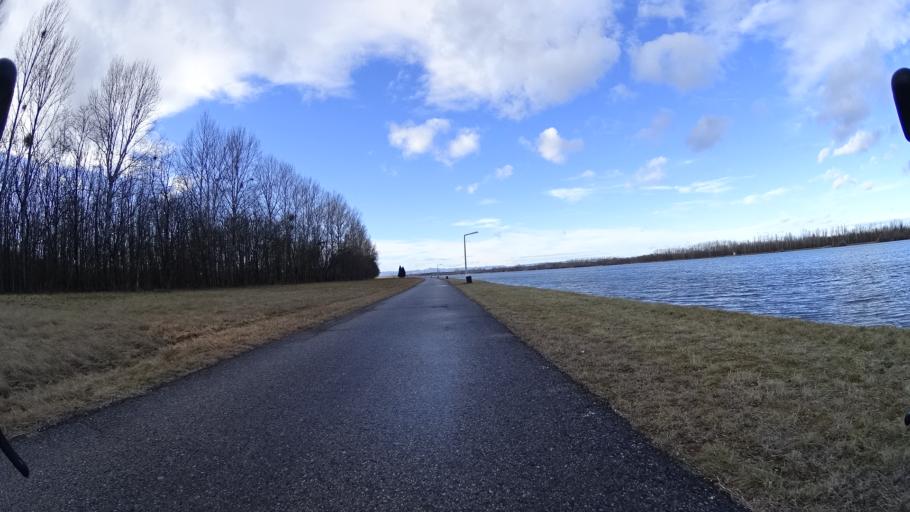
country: AT
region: Lower Austria
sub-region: Politischer Bezirk Tulln
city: Fels am Wagram
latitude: 48.3785
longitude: 15.8424
